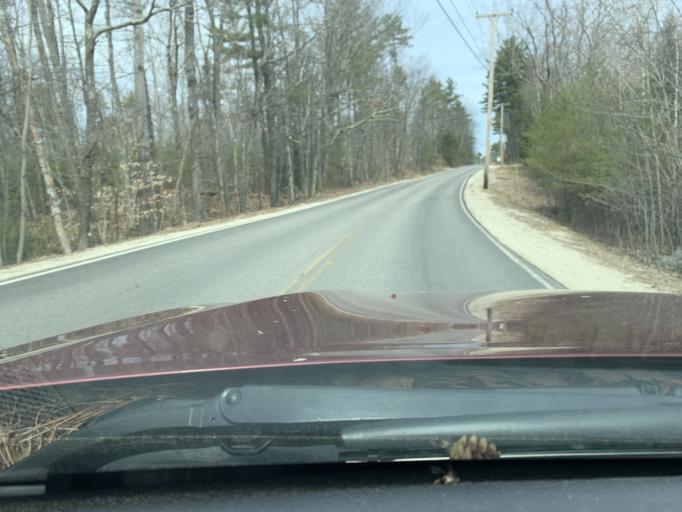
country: US
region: Maine
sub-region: Cumberland County
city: Raymond
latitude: 43.9375
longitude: -70.3816
